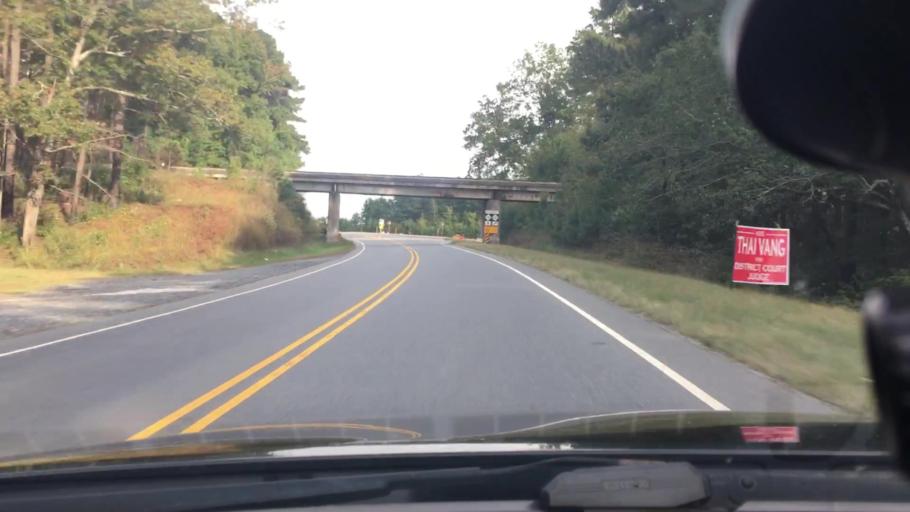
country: US
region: North Carolina
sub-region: Montgomery County
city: Troy
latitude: 35.3214
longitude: -79.9473
